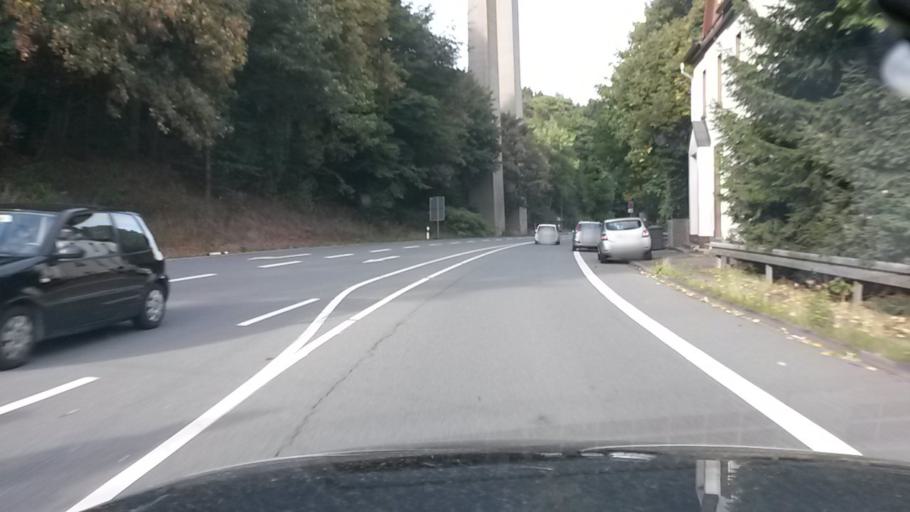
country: DE
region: North Rhine-Westphalia
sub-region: Regierungsbezirk Arnsberg
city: Luedenscheid
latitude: 51.2289
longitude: 7.6627
